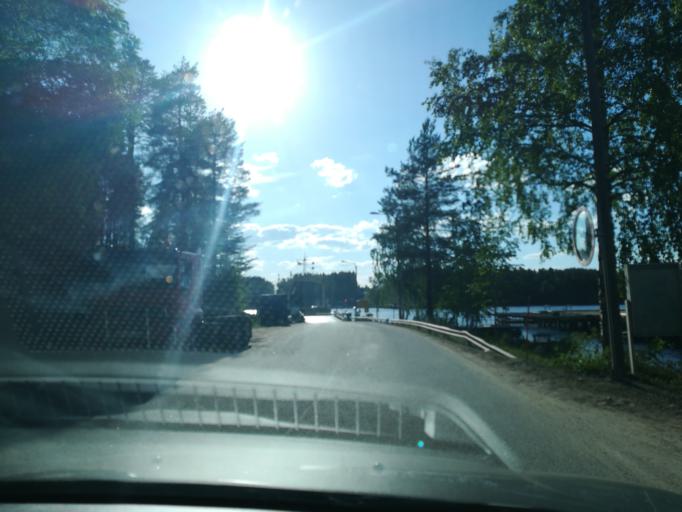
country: FI
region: Southern Savonia
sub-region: Savonlinna
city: Sulkava
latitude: 61.7378
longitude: 28.5045
